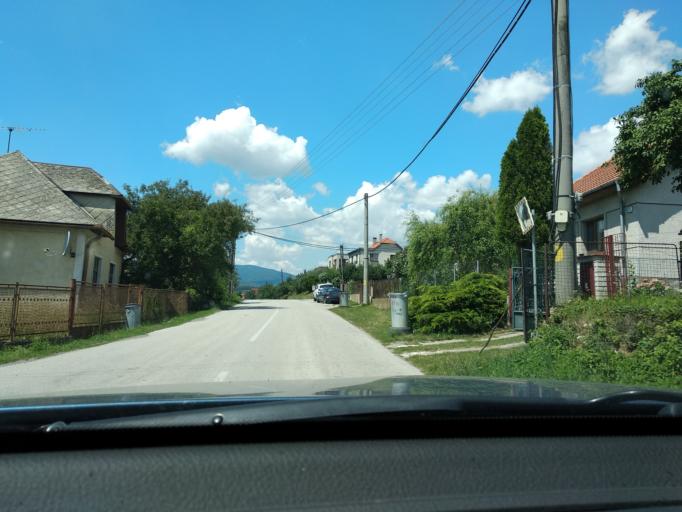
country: SK
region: Nitriansky
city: Banovce nad Bebravou
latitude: 48.7002
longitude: 18.1356
